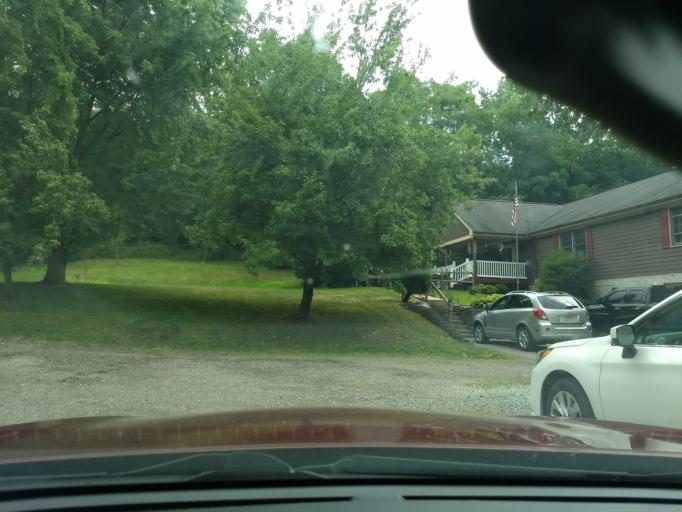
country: US
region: Pennsylvania
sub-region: Allegheny County
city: Bellevue
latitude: 40.4908
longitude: -80.0561
